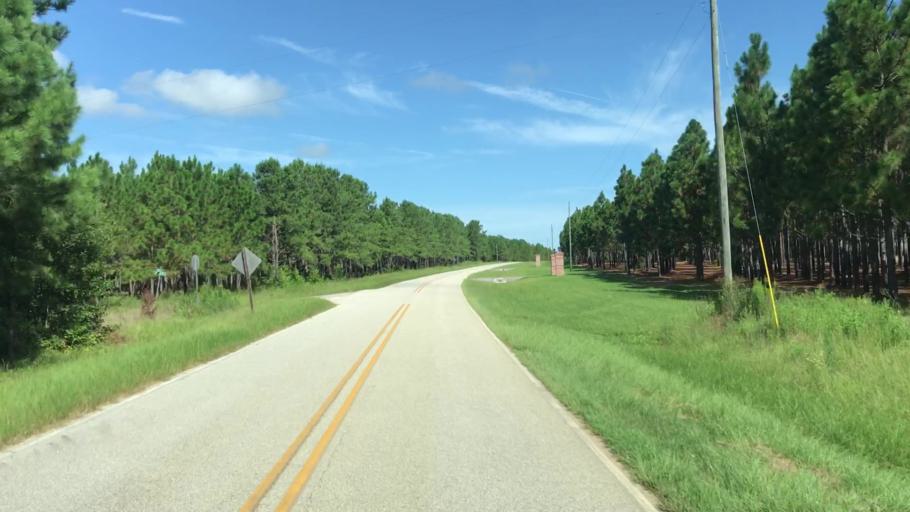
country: US
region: Georgia
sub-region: Jefferson County
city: Wadley
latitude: 32.8252
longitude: -82.3811
